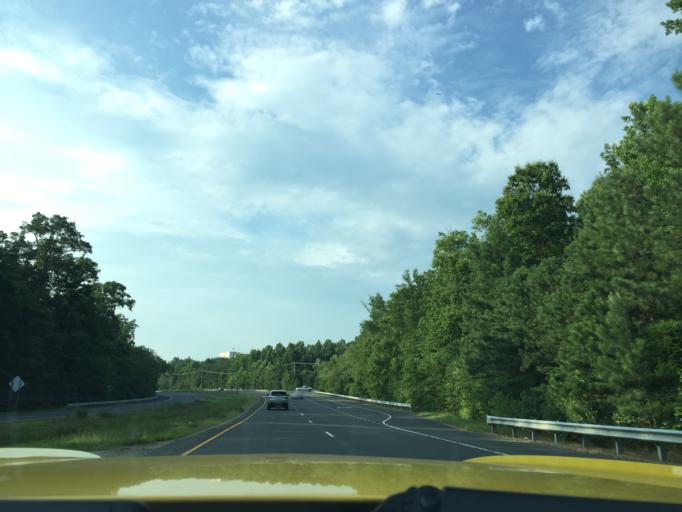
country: US
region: Virginia
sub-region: Fairfax County
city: Fort Belvoir
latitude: 38.7131
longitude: -77.1638
